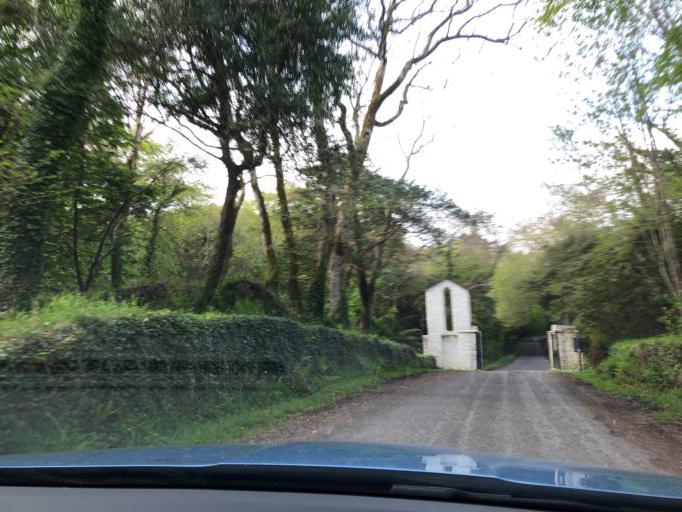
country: IE
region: Munster
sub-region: Ciarrai
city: Cahersiveen
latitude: 51.7632
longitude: -10.1320
